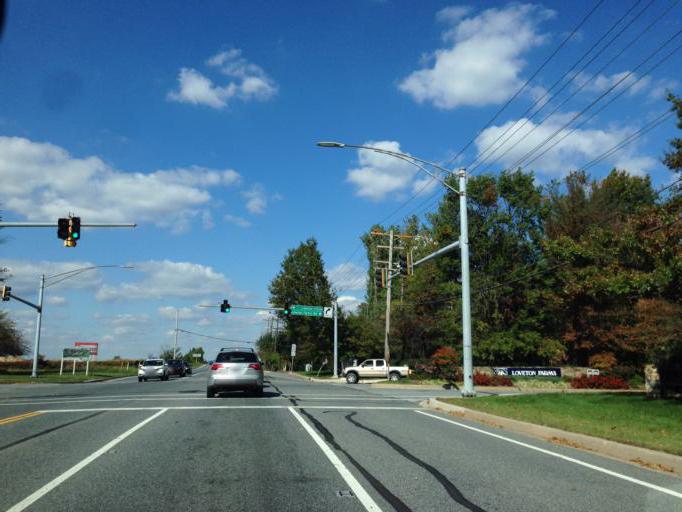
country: US
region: Maryland
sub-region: Baltimore County
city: Hunt Valley
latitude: 39.5199
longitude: -76.6431
